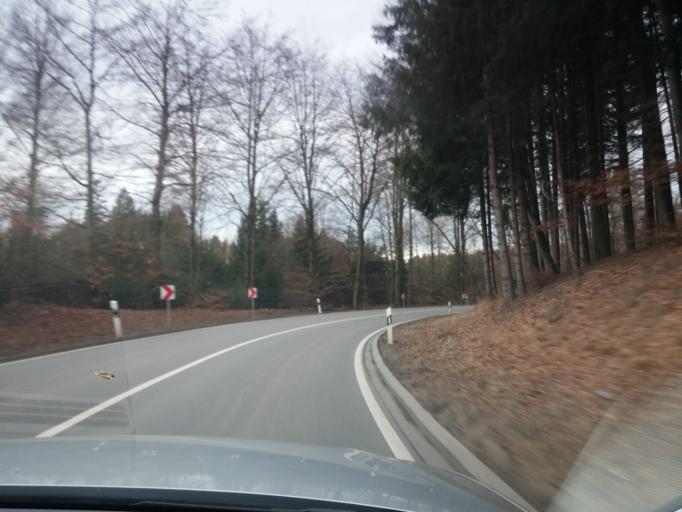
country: DE
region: Bavaria
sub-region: Upper Bavaria
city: Glonn
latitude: 47.9977
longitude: 11.8526
